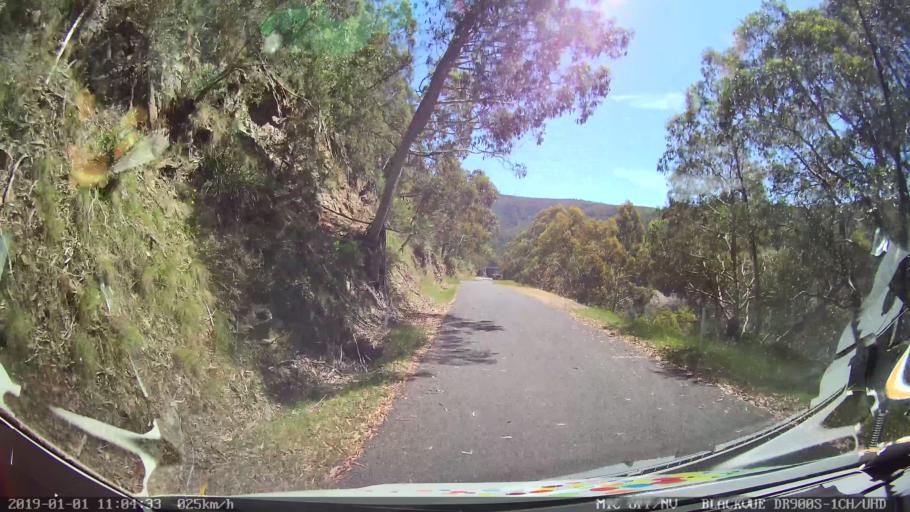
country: AU
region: New South Wales
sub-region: Snowy River
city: Jindabyne
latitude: -35.9694
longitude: 148.3888
